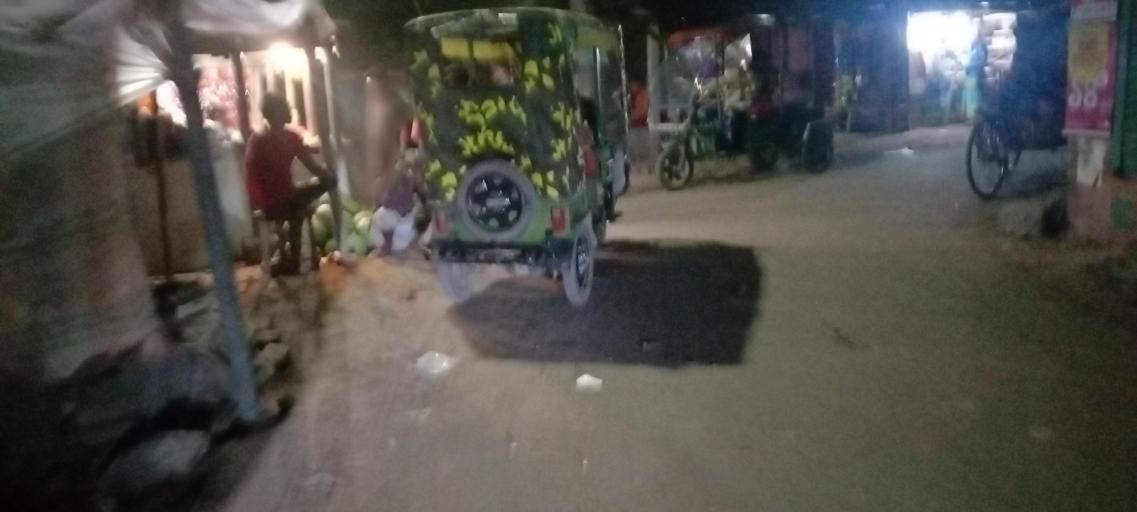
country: BD
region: Dhaka
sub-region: Dhaka
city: Dhaka
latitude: 23.6341
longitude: 90.4204
